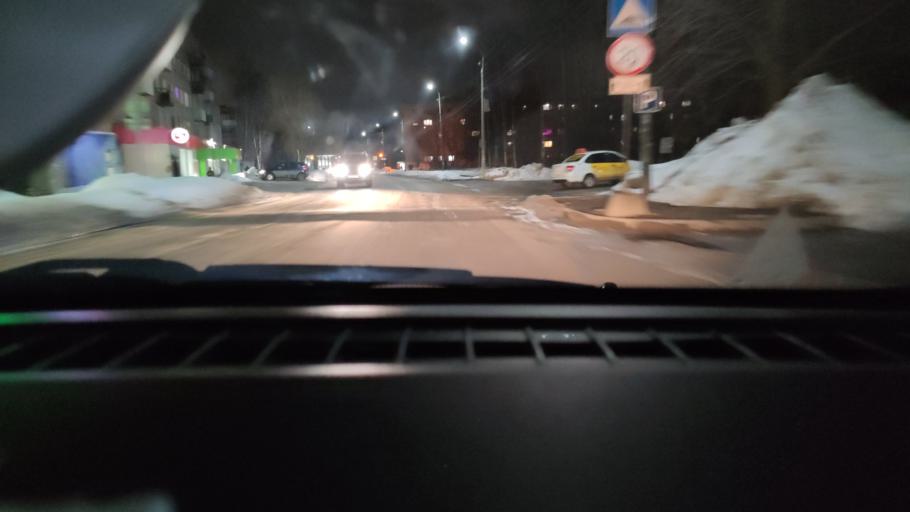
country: RU
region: Perm
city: Krasnokamsk
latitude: 58.0757
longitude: 55.7336
